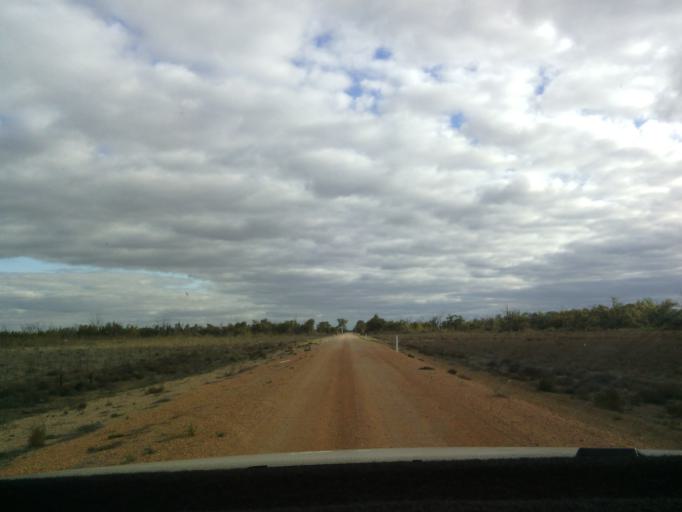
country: AU
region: South Australia
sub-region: Renmark Paringa
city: Renmark
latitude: -34.1642
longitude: 141.1952
